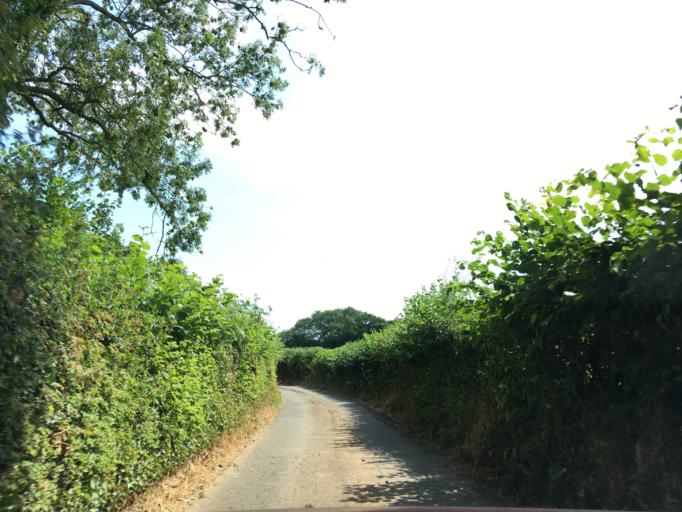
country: GB
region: Wales
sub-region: Monmouthshire
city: Magor
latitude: 51.5974
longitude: -2.8413
